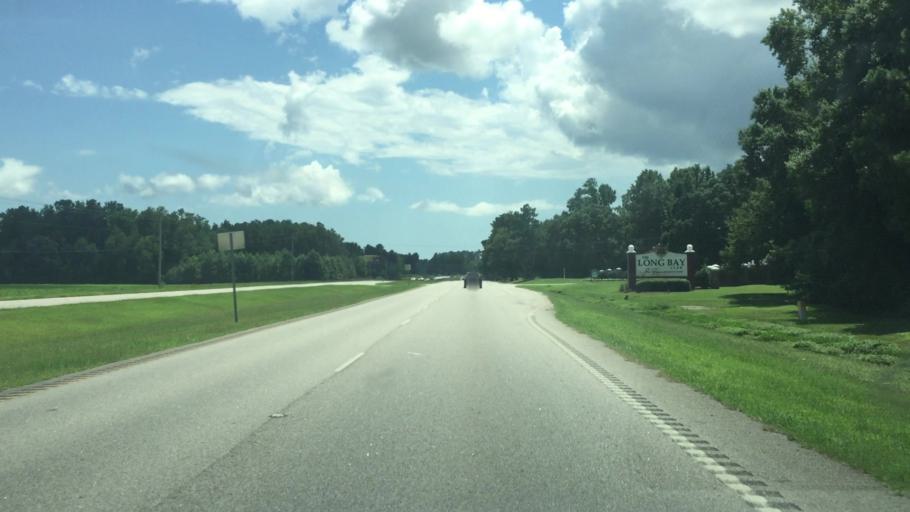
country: US
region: South Carolina
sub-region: Horry County
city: Little River
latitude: 33.9509
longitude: -78.7356
